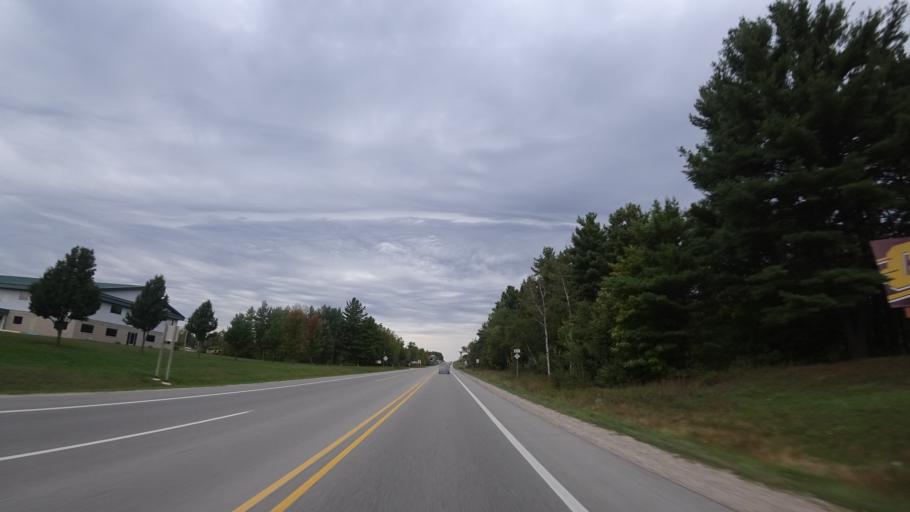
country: US
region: Michigan
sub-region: Antrim County
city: Elk Rapids
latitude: 44.7714
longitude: -85.4044
